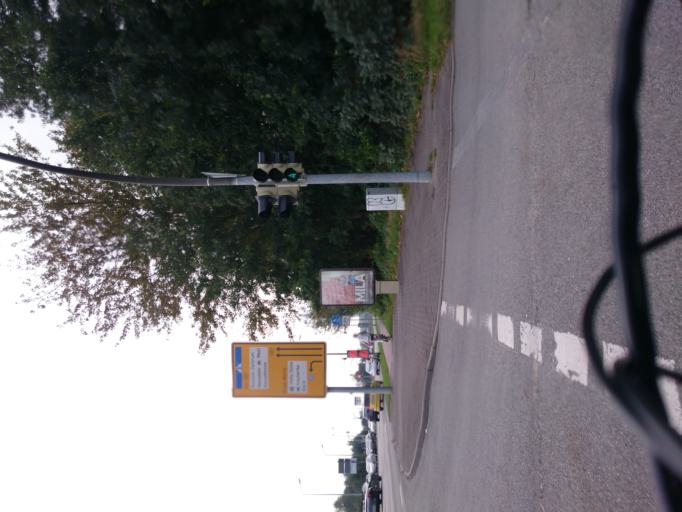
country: DE
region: Mecklenburg-Vorpommern
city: Warnemuende
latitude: 54.1690
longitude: 12.0800
